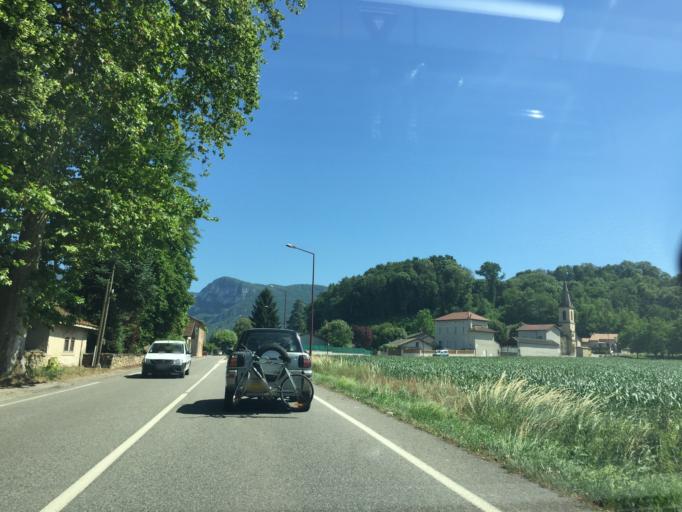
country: FR
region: Rhone-Alpes
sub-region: Departement de l'Isere
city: Saint-Just-de-Claix
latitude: 45.0505
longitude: 5.2935
